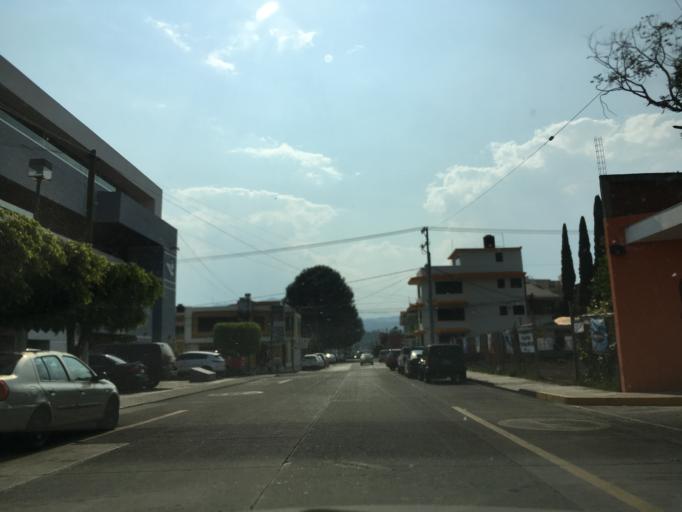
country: MX
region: Michoacan
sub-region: Uruapan
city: Uruapan
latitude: 19.4085
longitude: -102.0560
